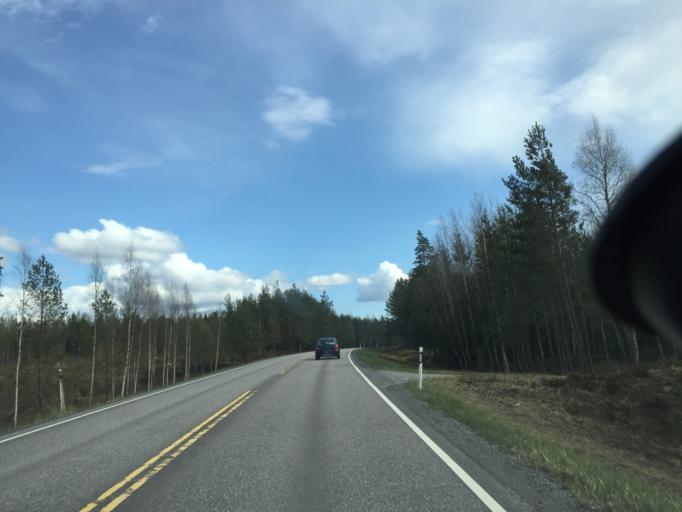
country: FI
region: Uusimaa
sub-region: Raaseporin
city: Ekenaes
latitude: 60.0373
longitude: 23.3613
